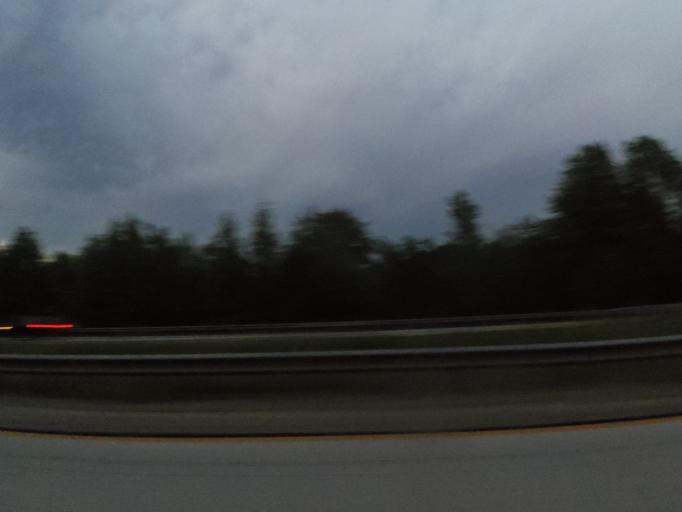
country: US
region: Georgia
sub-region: McDuffie County
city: Thomson
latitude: 33.5125
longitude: -82.4591
